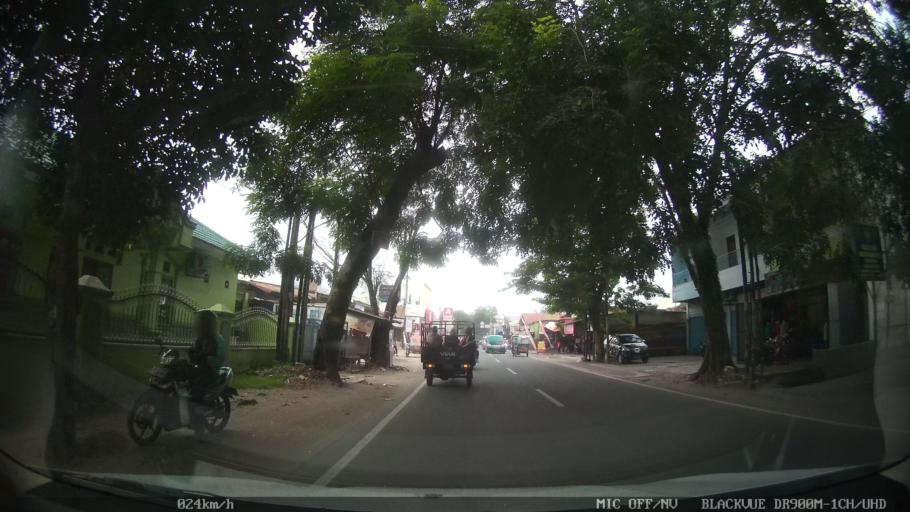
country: ID
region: North Sumatra
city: Medan
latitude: 3.5683
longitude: 98.7148
